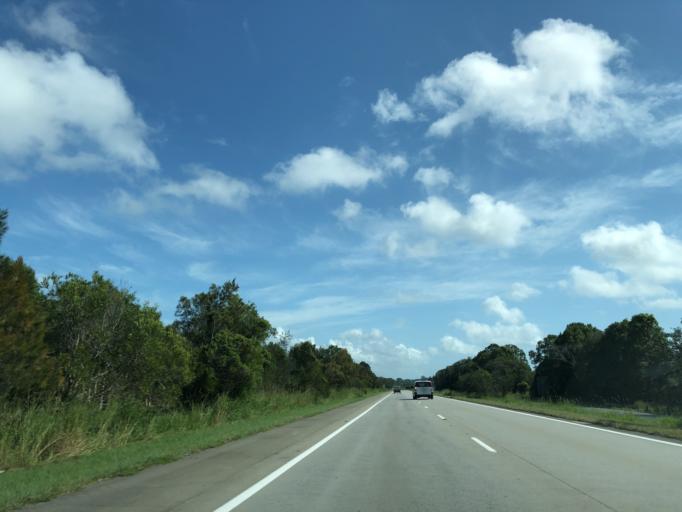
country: AU
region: New South Wales
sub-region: Byron Shire
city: Brunswick Heads
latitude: -28.5931
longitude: 153.5445
